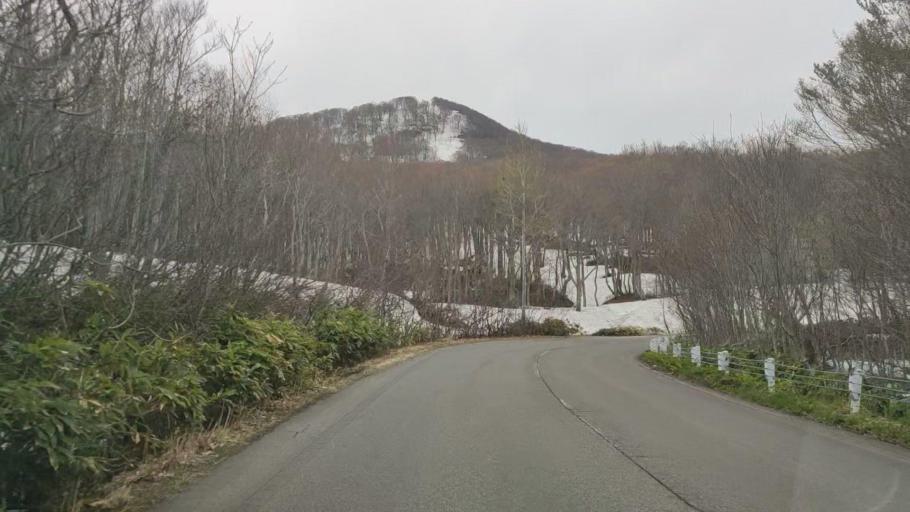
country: JP
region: Aomori
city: Aomori Shi
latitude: 40.6544
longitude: 140.9551
